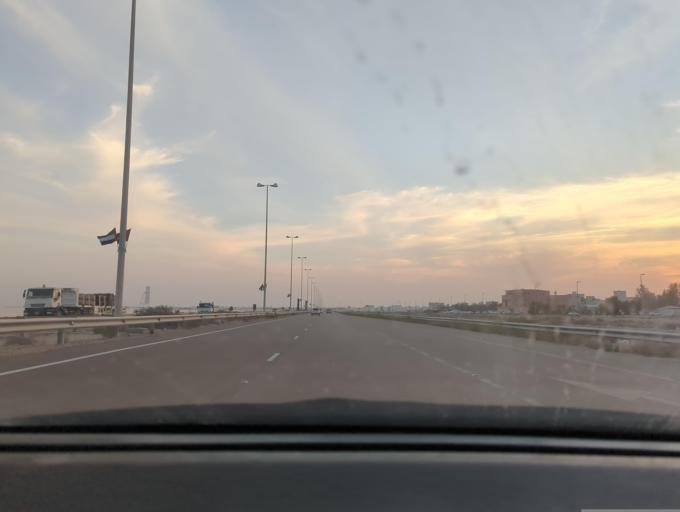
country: AE
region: Abu Dhabi
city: Abu Dhabi
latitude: 24.3401
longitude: 54.6539
